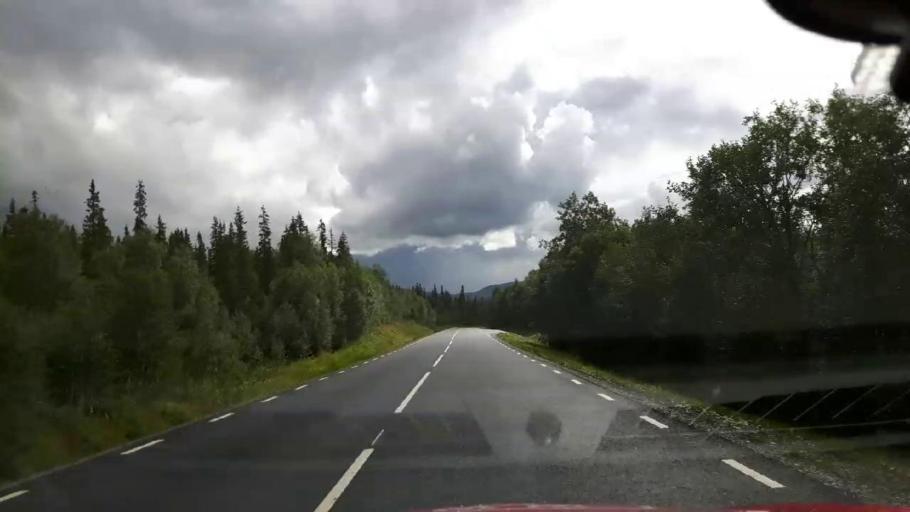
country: NO
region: Nord-Trondelag
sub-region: Royrvik
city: Royrvik
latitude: 64.8805
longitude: 14.2110
